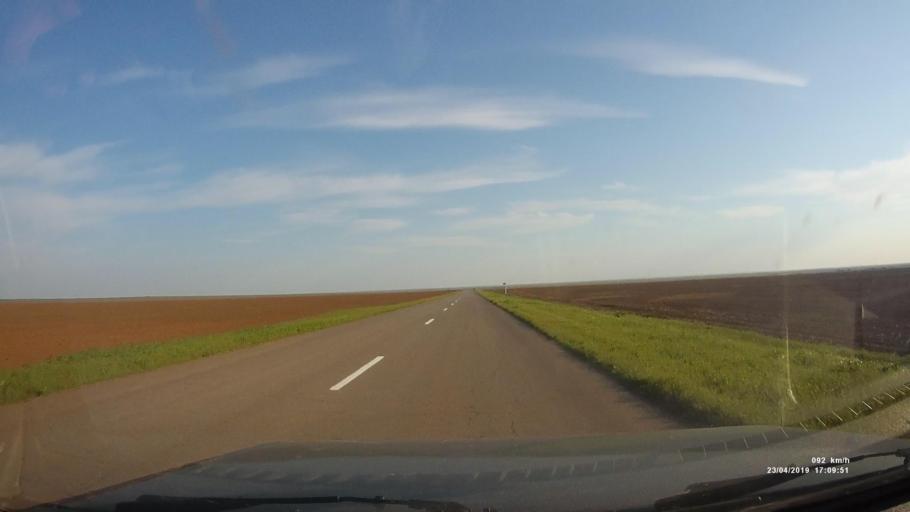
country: RU
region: Kalmykiya
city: Priyutnoye
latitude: 46.2530
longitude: 43.4842
